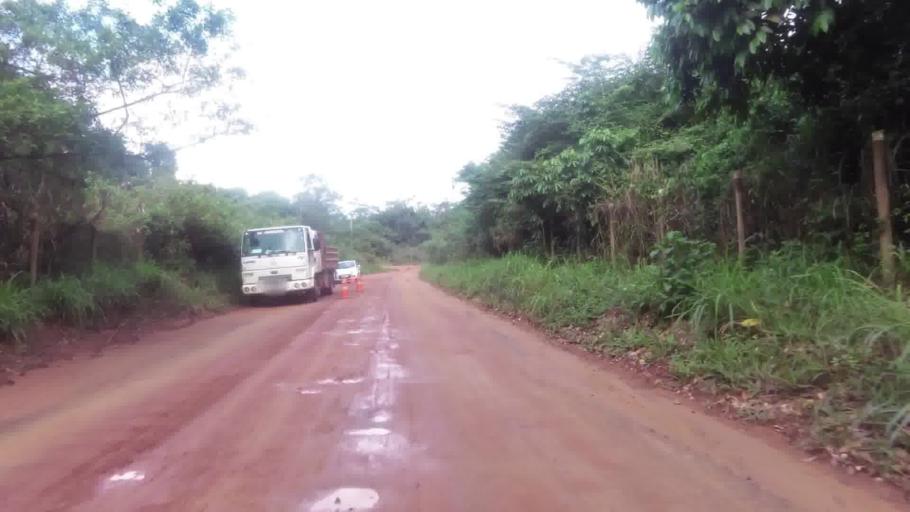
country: BR
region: Espirito Santo
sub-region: Piuma
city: Piuma
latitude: -20.7926
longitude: -40.6347
